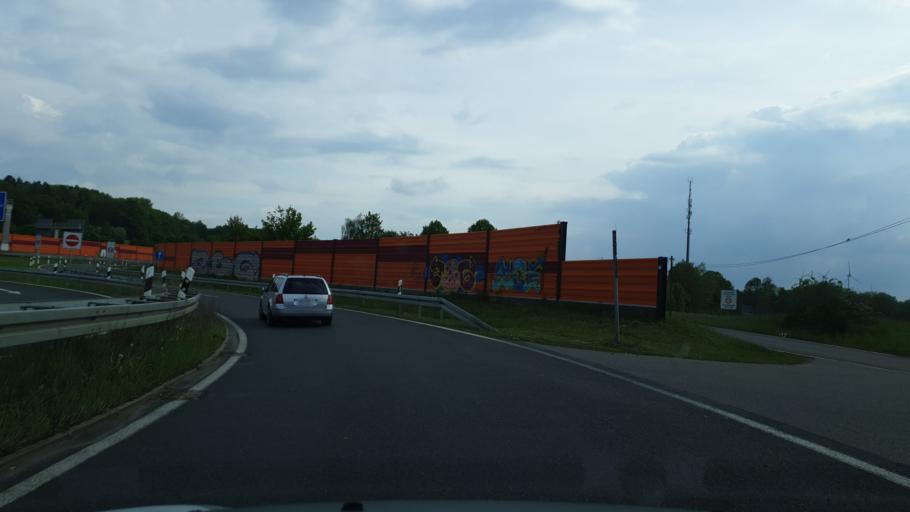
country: DE
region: Saxony
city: Wittgensdorf
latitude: 50.8598
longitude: 12.8649
